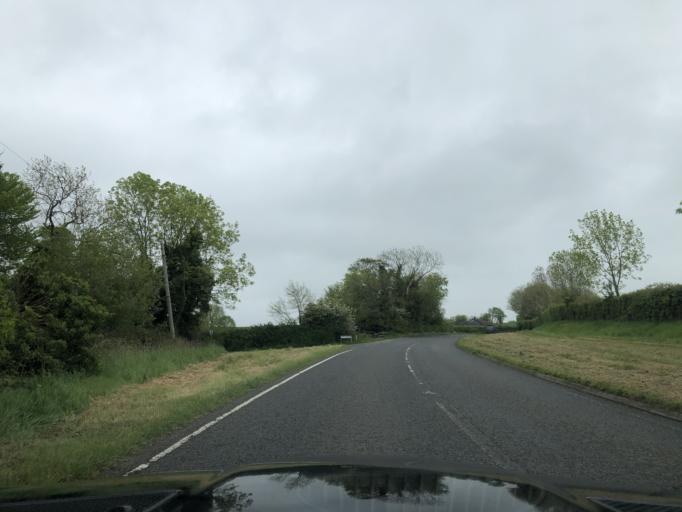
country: GB
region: Northern Ireland
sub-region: Down District
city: Killyleagh
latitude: 54.3572
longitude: -5.6670
